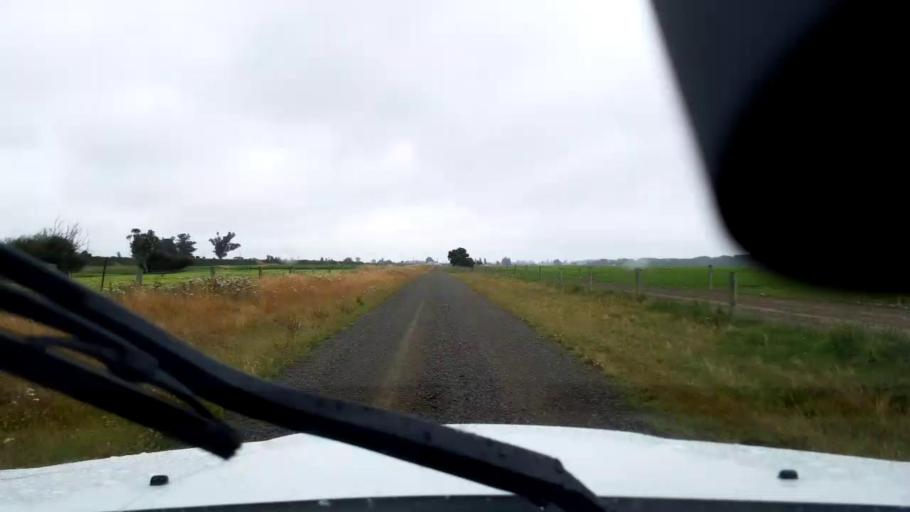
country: NZ
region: Canterbury
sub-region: Timaru District
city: Pleasant Point
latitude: -44.2539
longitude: 171.1922
